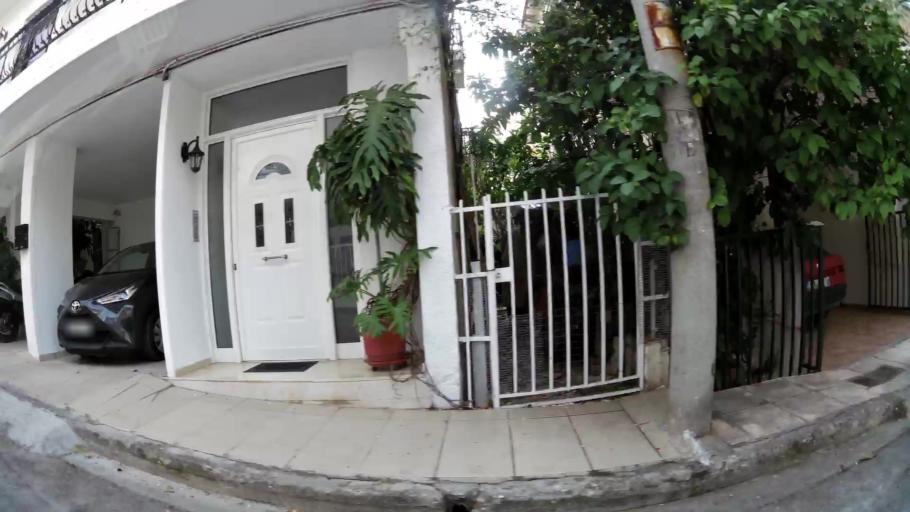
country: GR
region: Attica
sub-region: Nomarchia Athinas
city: Agios Dimitrios
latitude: 37.9246
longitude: 23.7257
